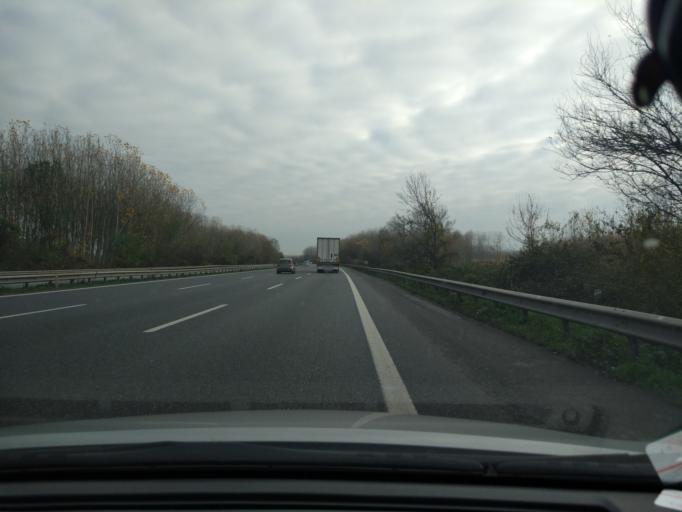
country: TR
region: Sakarya
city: Karapurcek
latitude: 40.7114
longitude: 30.5109
